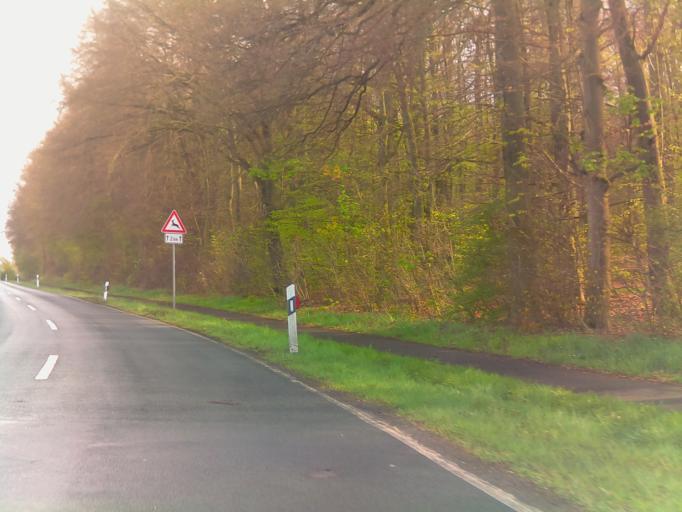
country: DE
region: Hesse
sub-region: Regierungsbezirk Giessen
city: Wetzlar
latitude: 50.5359
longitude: 8.5290
